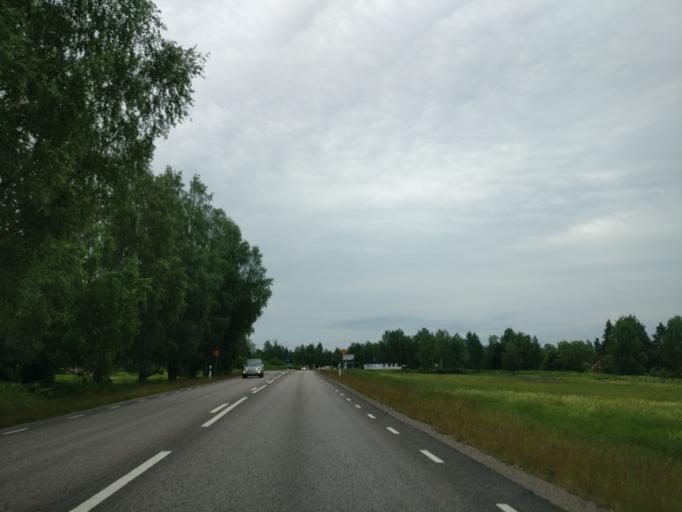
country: SE
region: Vaermland
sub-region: Hagfors Kommun
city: Hagfors
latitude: 60.0281
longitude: 13.6120
